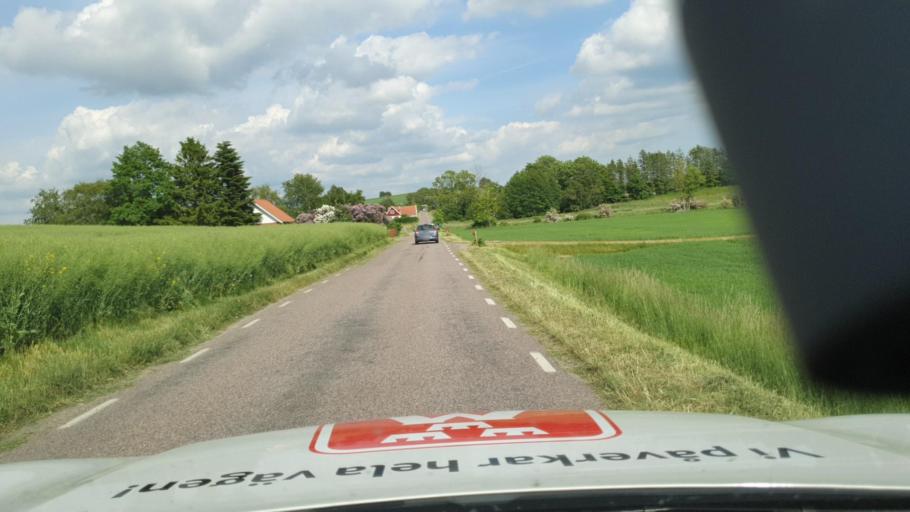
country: SE
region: Skane
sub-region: Skurups Kommun
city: Skurup
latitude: 55.5160
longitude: 13.5263
